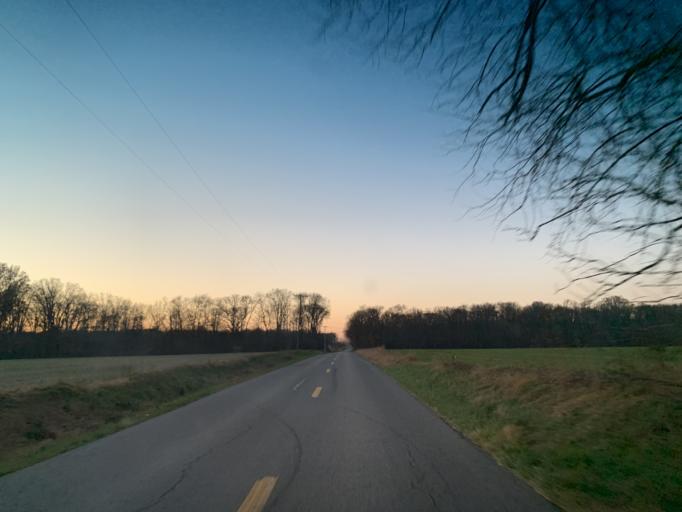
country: US
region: Delaware
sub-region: New Castle County
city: Middletown
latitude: 39.4125
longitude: -75.7573
